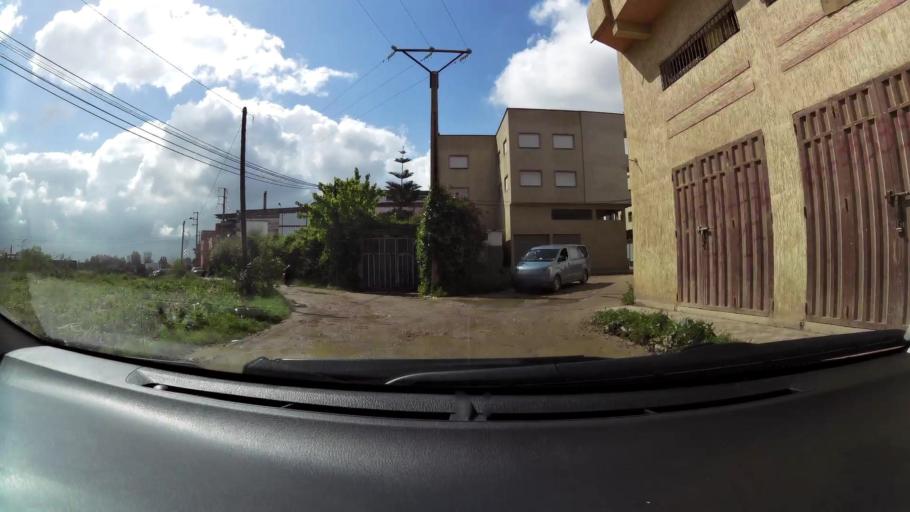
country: MA
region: Grand Casablanca
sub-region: Mediouna
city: Tit Mellil
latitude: 33.5442
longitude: -7.4895
